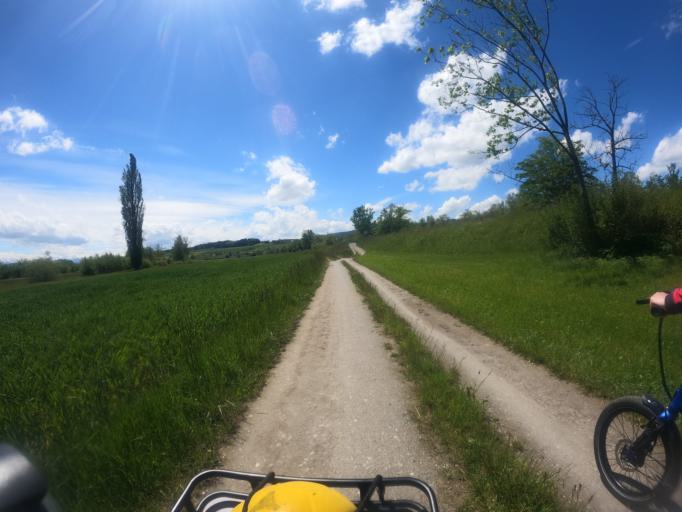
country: CH
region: Zurich
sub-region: Bezirk Affoltern
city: Obfelden / Oberlunnern
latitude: 47.2349
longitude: 8.4046
